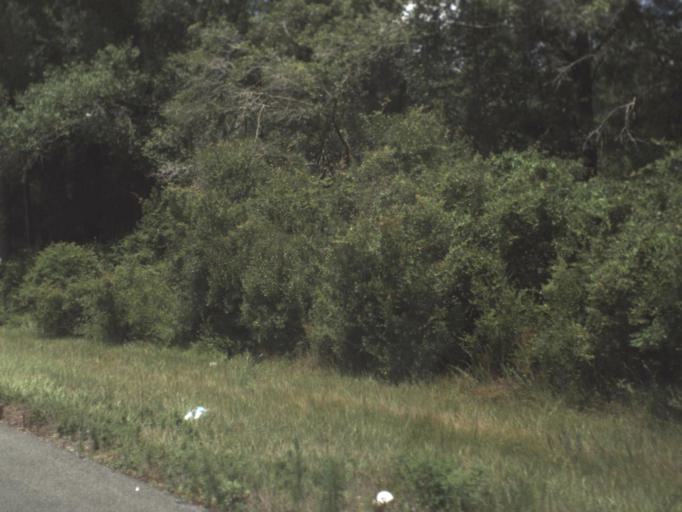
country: US
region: Florida
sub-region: Taylor County
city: Perry
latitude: 30.0896
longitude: -83.6474
